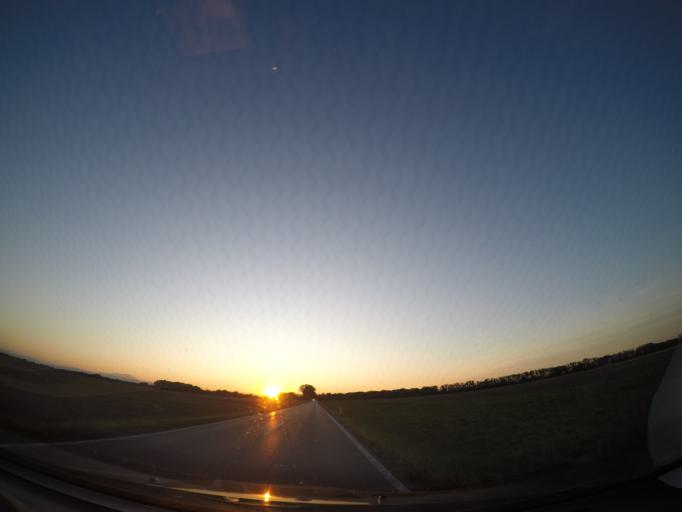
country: AT
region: Lower Austria
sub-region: Politischer Bezirk Baden
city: Mitterndorf an der Fischa
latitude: 47.9614
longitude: 16.4798
